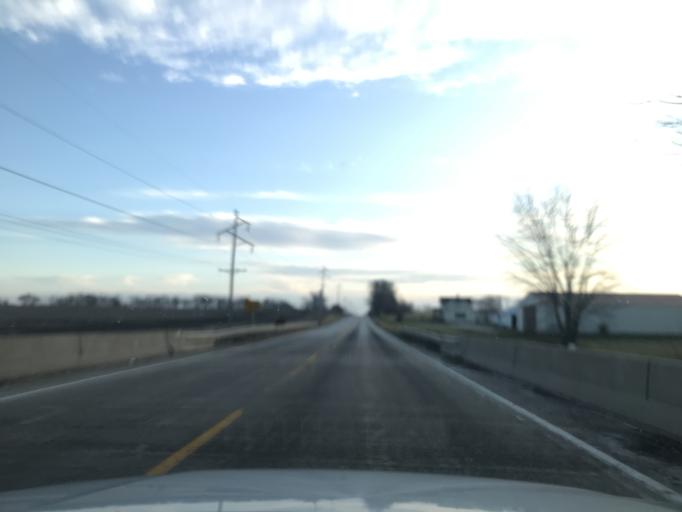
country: US
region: Illinois
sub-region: Mercer County
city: Aledo
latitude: 41.0429
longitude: -90.7459
